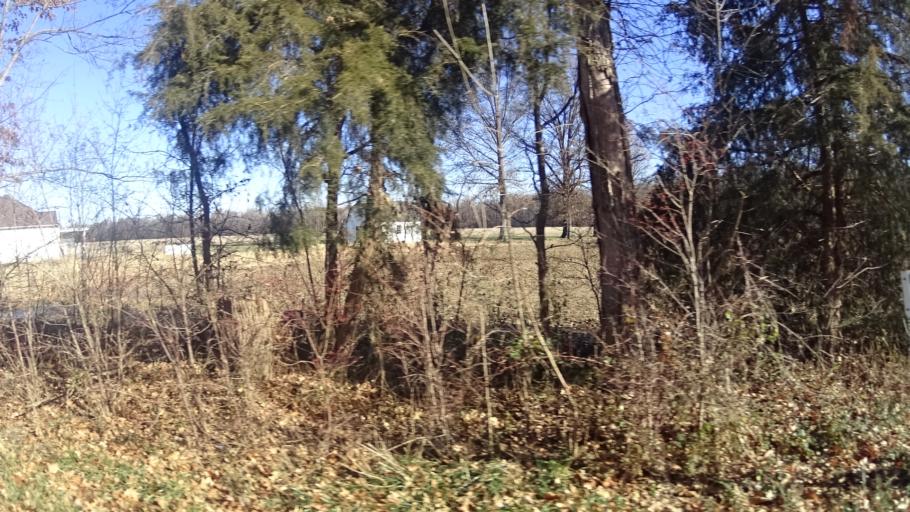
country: US
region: Ohio
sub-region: Lorain County
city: Vermilion-on-the-Lake
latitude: 41.3757
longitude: -82.3076
